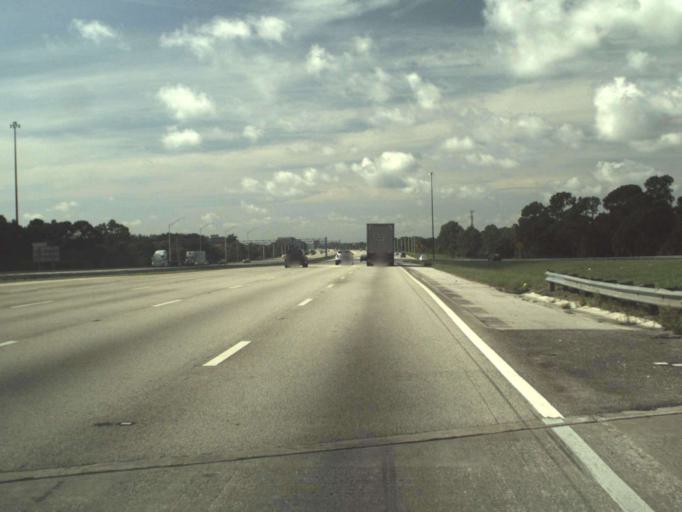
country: US
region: Florida
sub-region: Palm Beach County
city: Limestone Creek
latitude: 26.9293
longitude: -80.1490
